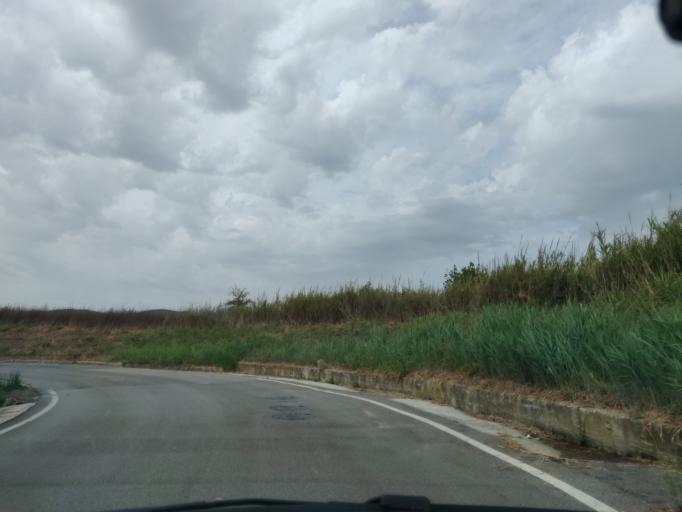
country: IT
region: Latium
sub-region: Citta metropolitana di Roma Capitale
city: Santa Marinella
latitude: 42.0393
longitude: 11.9188
